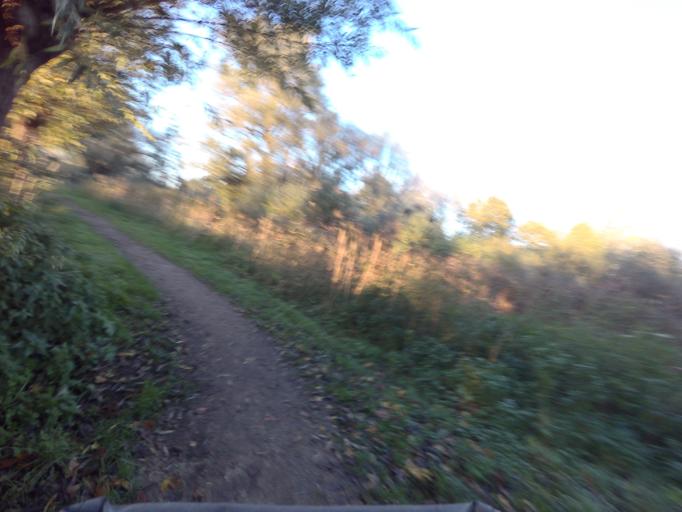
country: NL
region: North Brabant
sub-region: Gemeente Woudrichem
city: Woudrichem
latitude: 51.7892
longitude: 5.0225
